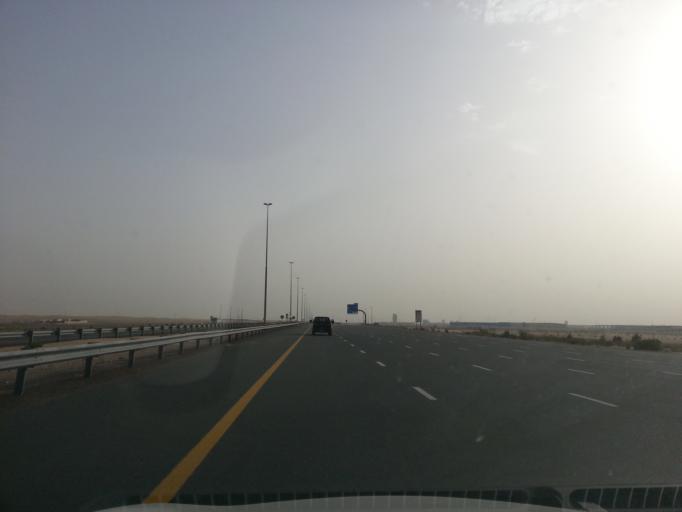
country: AE
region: Dubai
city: Dubai
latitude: 24.8174
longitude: 55.1153
